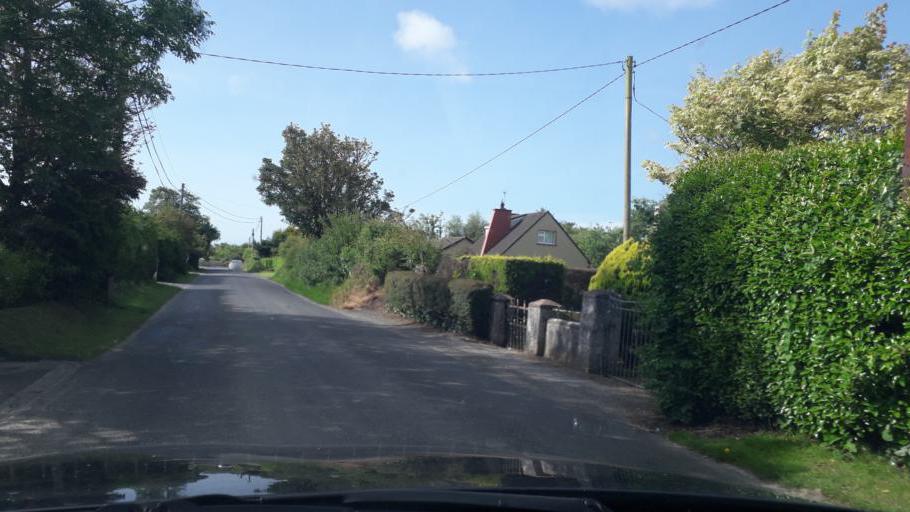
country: IE
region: Leinster
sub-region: Loch Garman
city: Loch Garman
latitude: 52.2437
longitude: -6.5504
